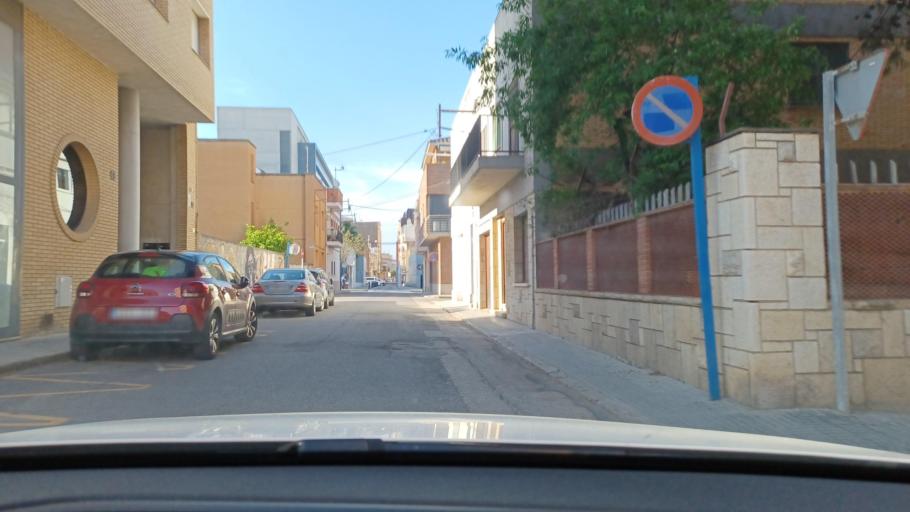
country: ES
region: Catalonia
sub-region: Provincia de Tarragona
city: Amposta
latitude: 40.7081
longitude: 0.5763
